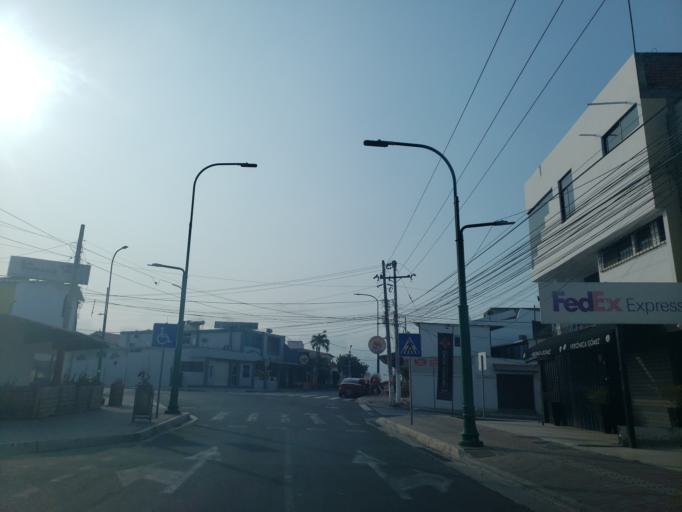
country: EC
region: Manabi
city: Manta
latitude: -0.9444
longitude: -80.7405
